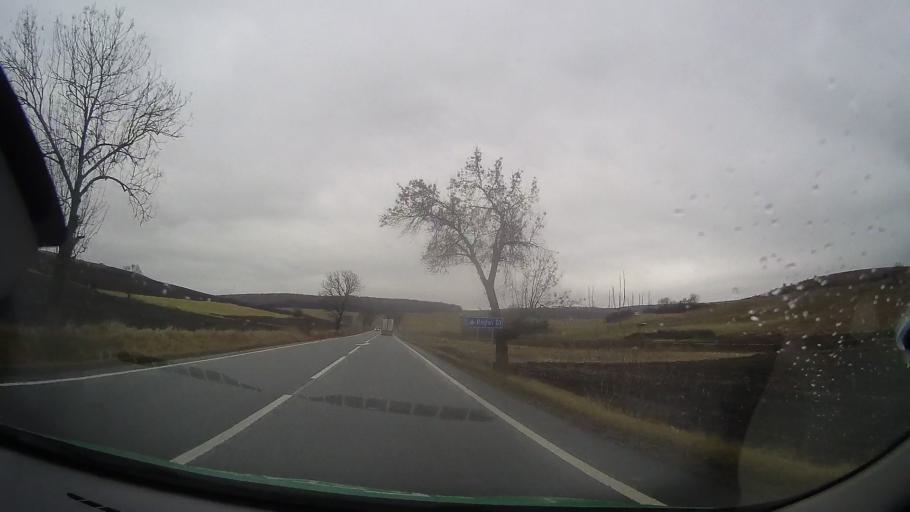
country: RO
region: Mures
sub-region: Comuna Lunca
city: Lunca
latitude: 46.8671
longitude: 24.5538
